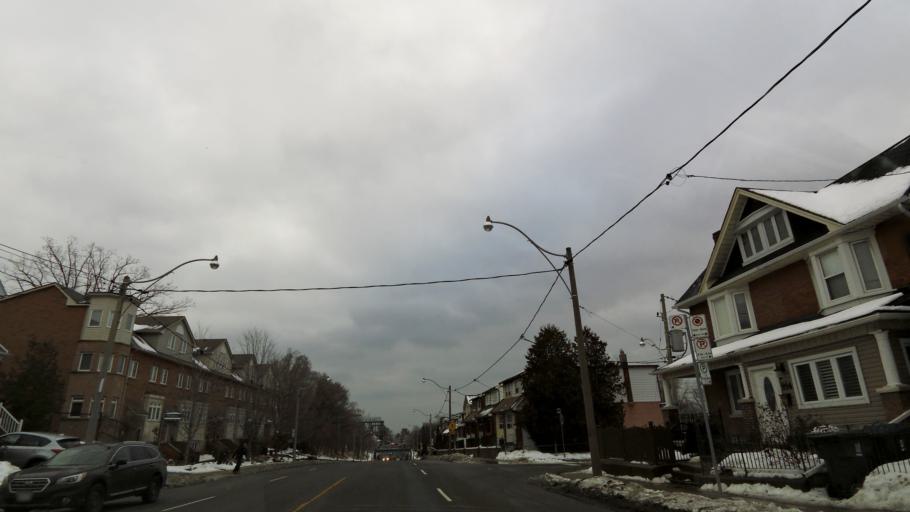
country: CA
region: Ontario
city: Scarborough
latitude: 43.6846
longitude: -79.3124
